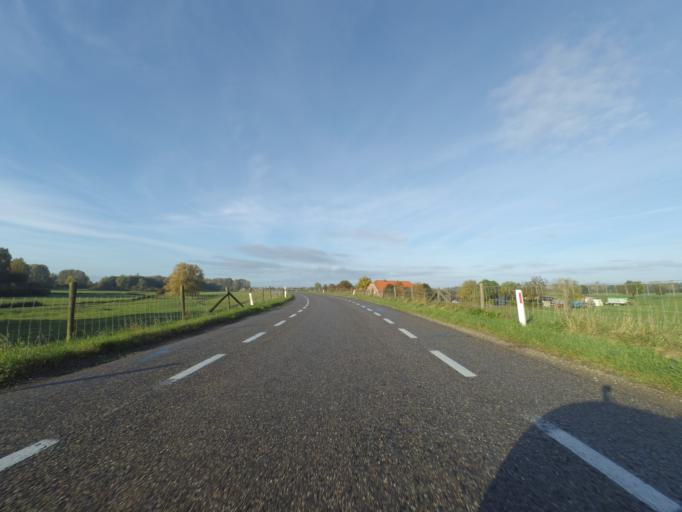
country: NL
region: Utrecht
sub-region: Gemeente Wijk bij Duurstede
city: Wijk bij Duurstede
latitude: 51.9786
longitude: 5.3738
